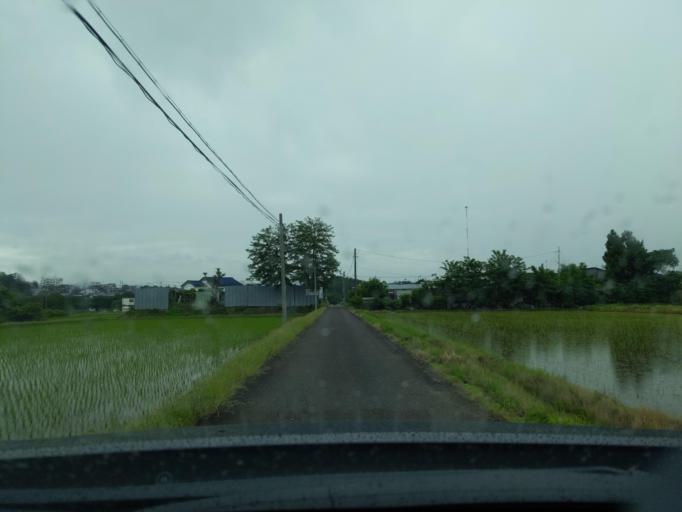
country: JP
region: Fukushima
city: Koriyama
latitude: 37.3675
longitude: 140.3543
